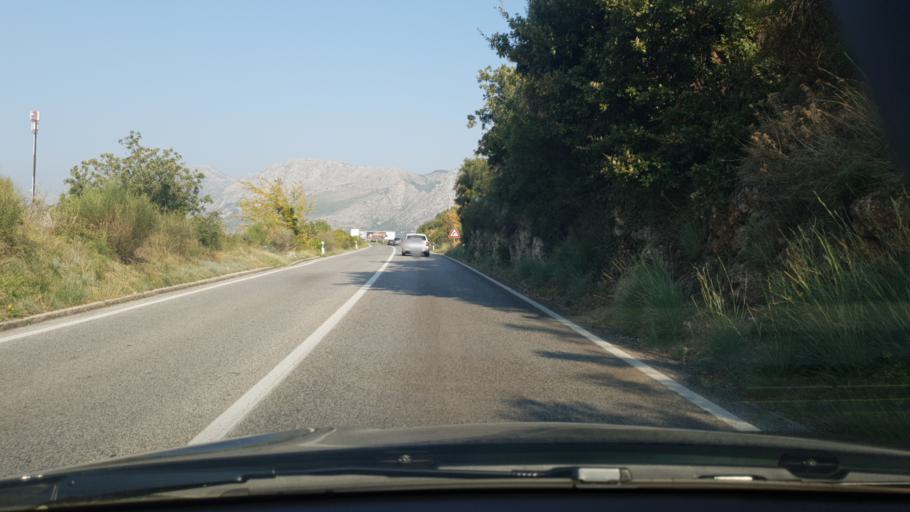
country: HR
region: Dubrovacko-Neretvanska
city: Cavtat
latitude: 42.5915
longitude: 18.2301
